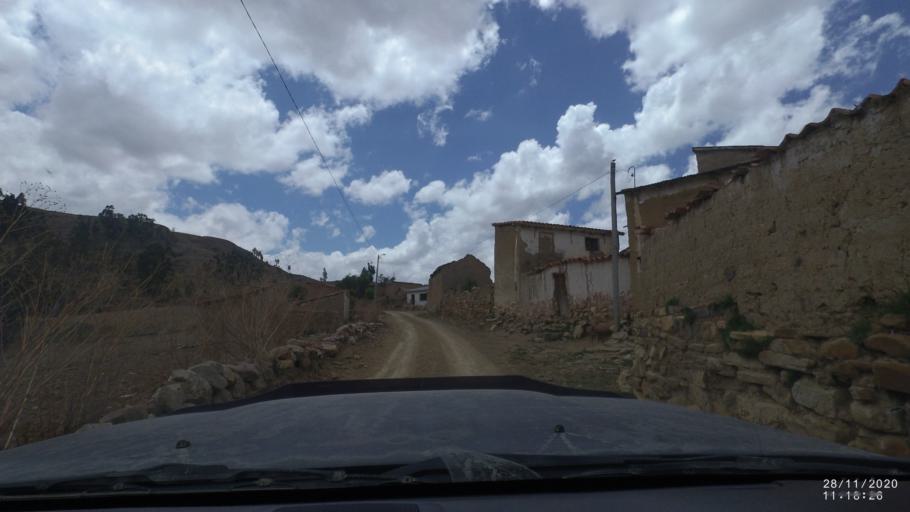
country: BO
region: Cochabamba
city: Tarata
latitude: -17.7534
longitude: -66.0738
